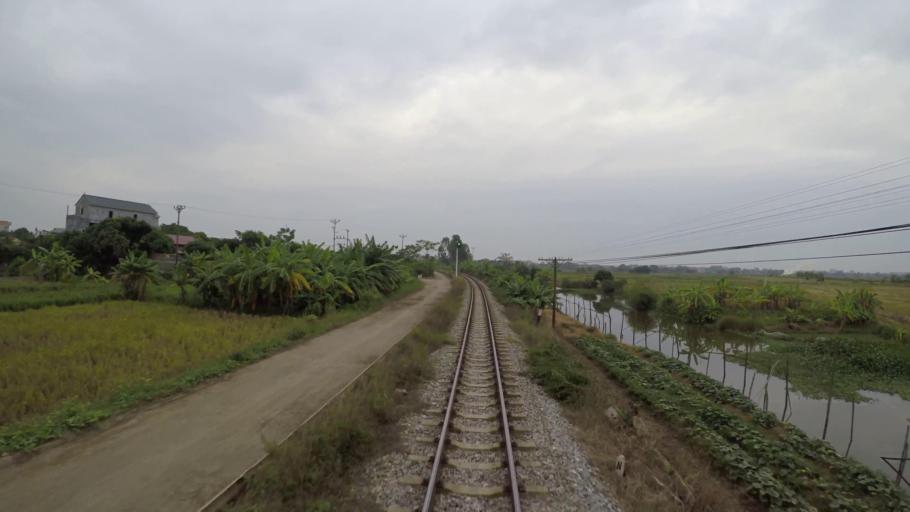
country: VN
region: Hai Duong
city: Ke Sat
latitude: 20.9659
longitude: 106.1346
